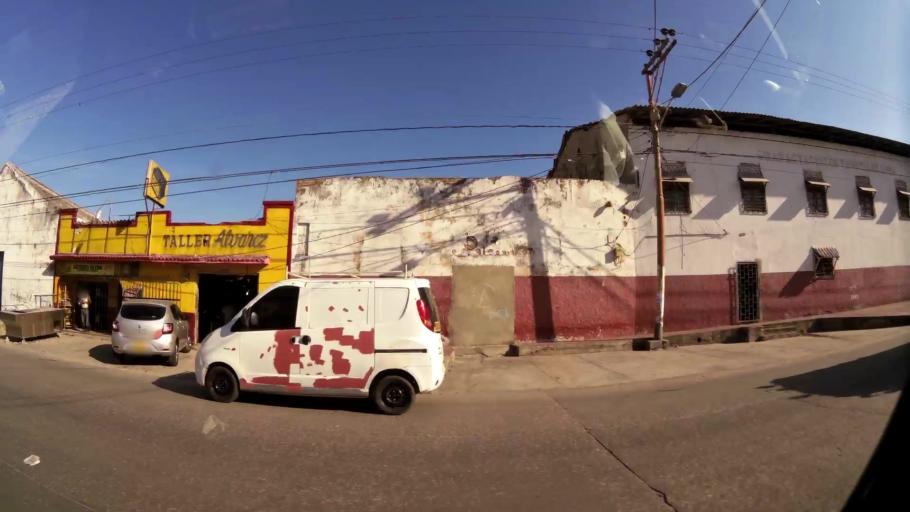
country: CO
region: Atlantico
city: Barranquilla
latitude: 10.9656
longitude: -74.7903
